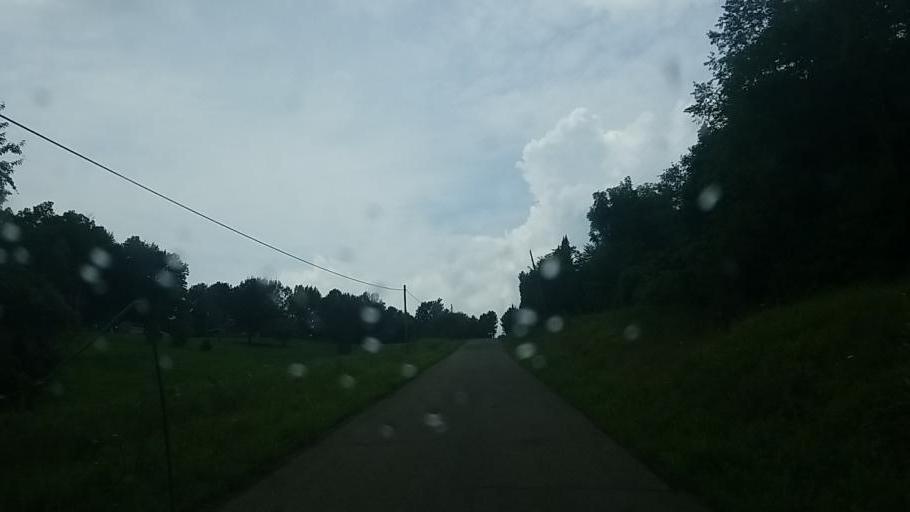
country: US
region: Ohio
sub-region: Muskingum County
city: Frazeysburg
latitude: 40.1589
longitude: -82.2682
